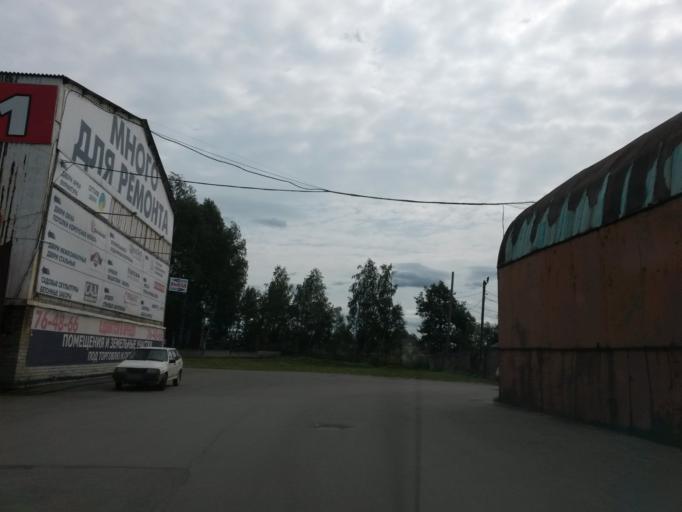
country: RU
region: Jaroslavl
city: Yaroslavl
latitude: 57.6867
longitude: 39.9065
